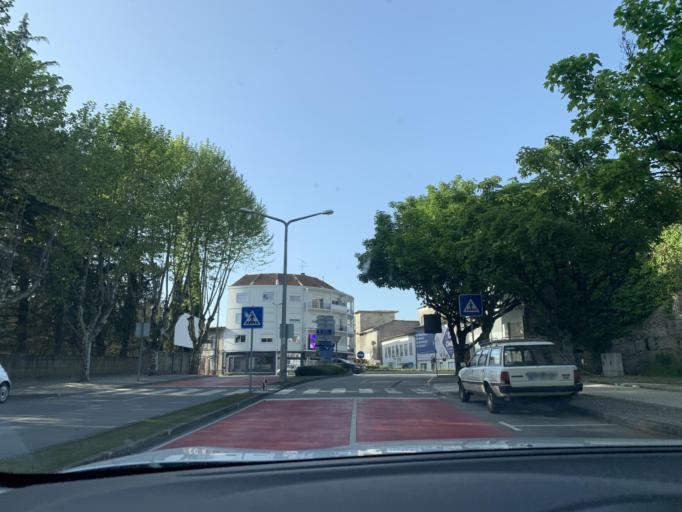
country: PT
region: Viseu
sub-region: Mangualde
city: Mangualde
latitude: 40.6044
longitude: -7.7622
